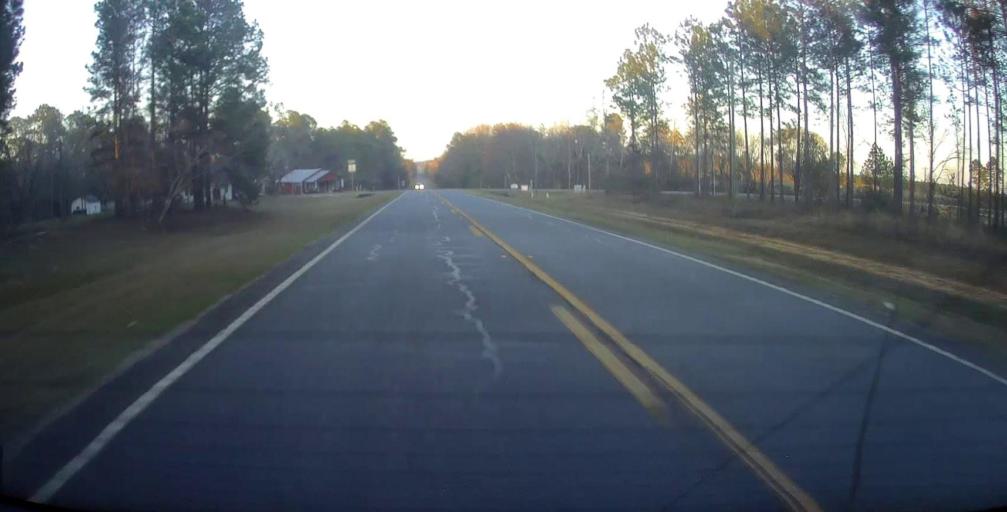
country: US
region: Georgia
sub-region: Dodge County
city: Eastman
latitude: 32.2818
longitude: -83.1059
